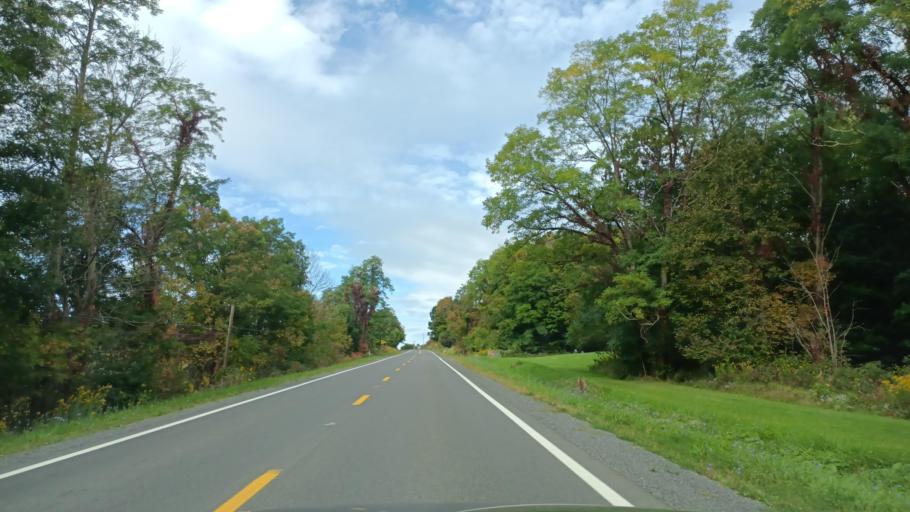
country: US
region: Maryland
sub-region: Garrett County
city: Mountain Lake Park
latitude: 39.2715
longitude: -79.2684
